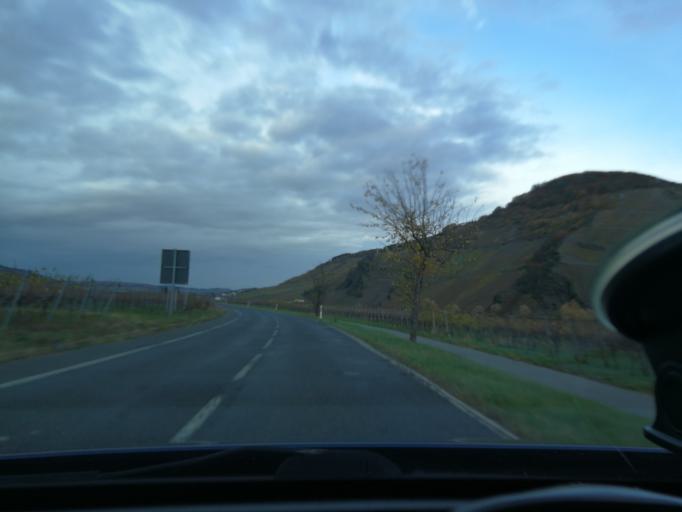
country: DE
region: Rheinland-Pfalz
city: Minheim
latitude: 49.8673
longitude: 6.9425
